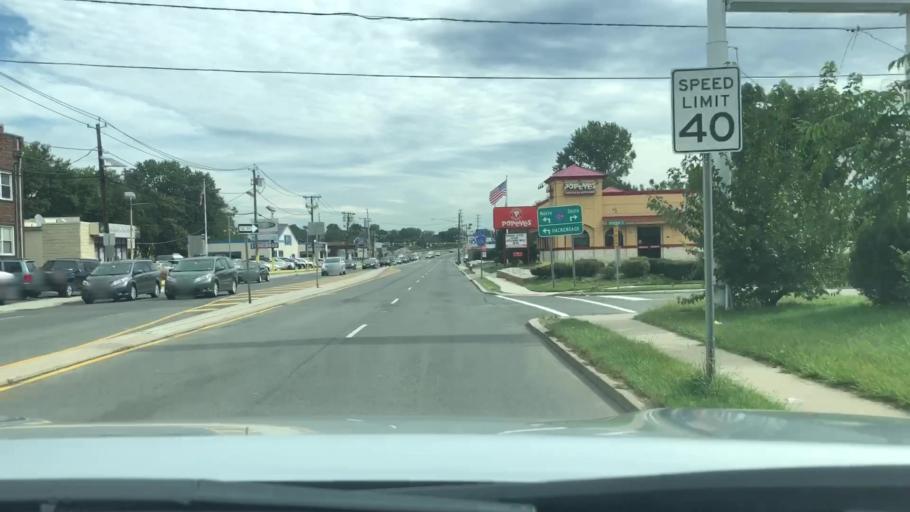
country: US
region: New Jersey
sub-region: Bergen County
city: Little Ferry
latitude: 40.8536
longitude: -74.0374
